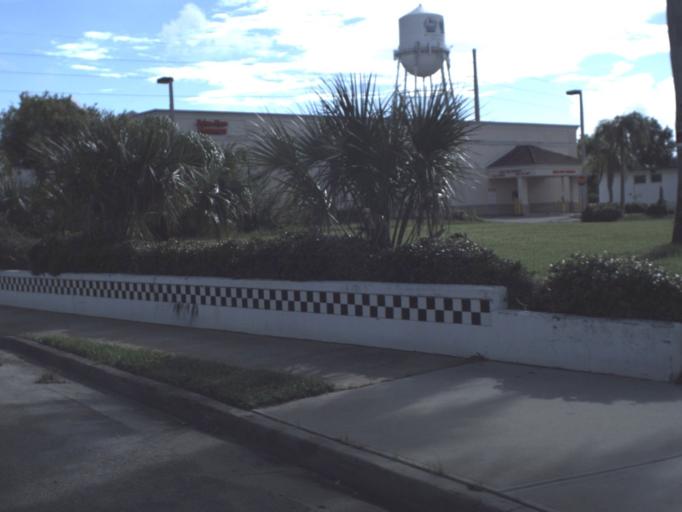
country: US
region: Florida
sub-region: Manatee County
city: Bradenton
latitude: 27.4950
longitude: -82.5631
